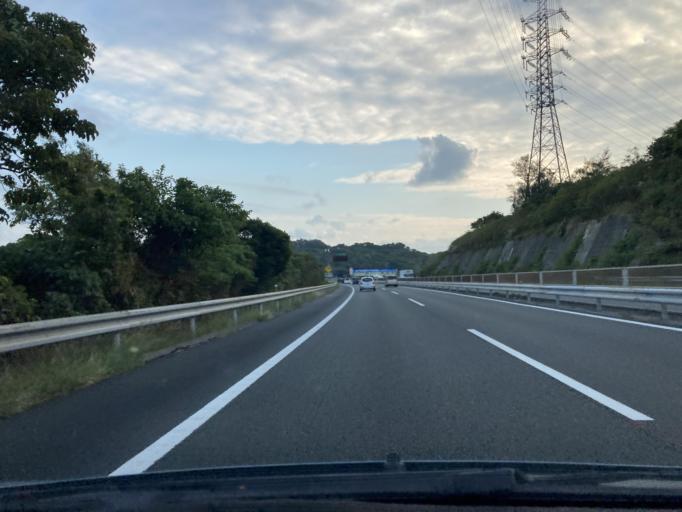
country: JP
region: Okinawa
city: Chatan
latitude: 26.3134
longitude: 127.7882
